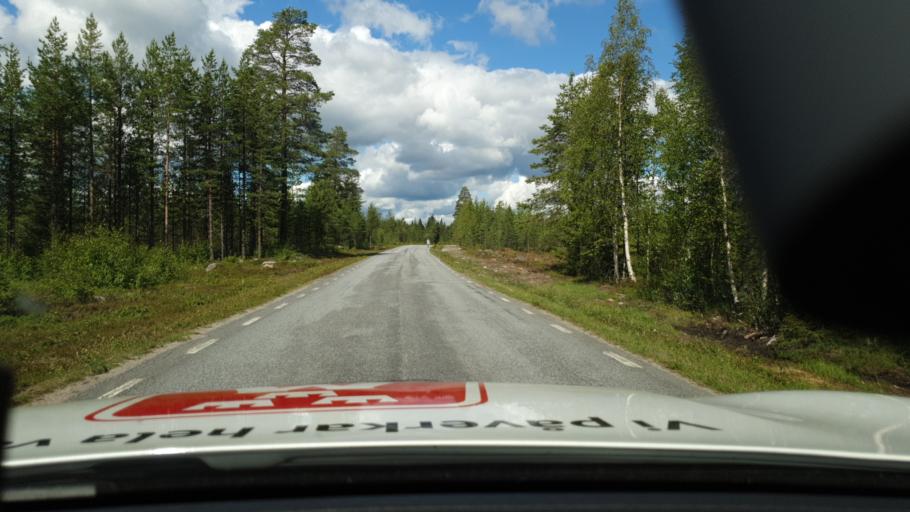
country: SE
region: Norrbotten
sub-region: Lulea Kommun
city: Ranea
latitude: 65.8321
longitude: 22.3133
